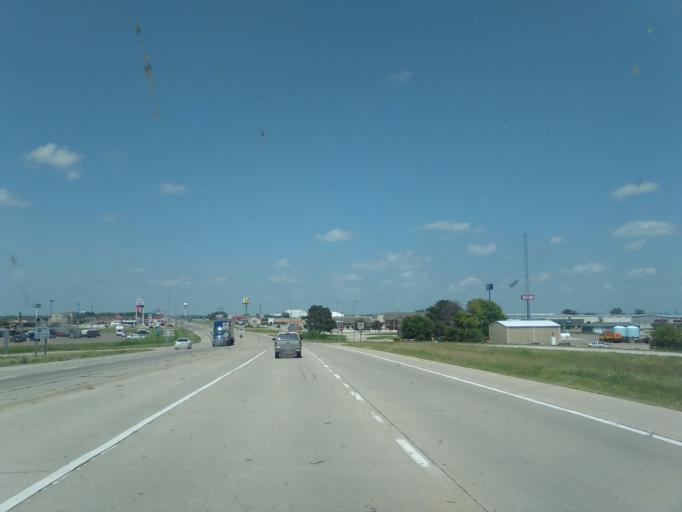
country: US
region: Nebraska
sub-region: Dawson County
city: Lexington
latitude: 40.7426
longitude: -99.7406
